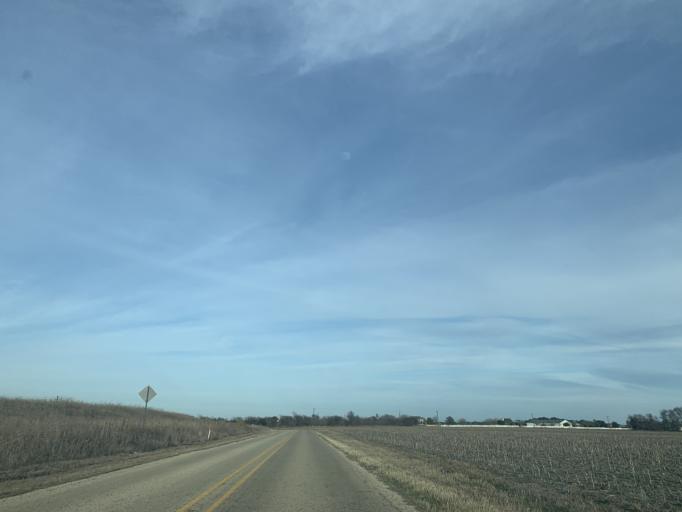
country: US
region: Texas
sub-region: Bell County
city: Salado
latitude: 30.9757
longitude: -97.5112
